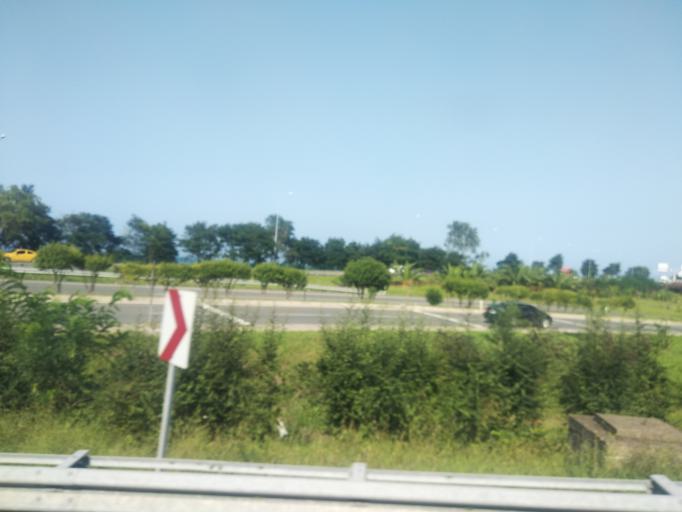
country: TR
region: Ordu
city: Ordu
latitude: 41.0175
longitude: 37.8436
